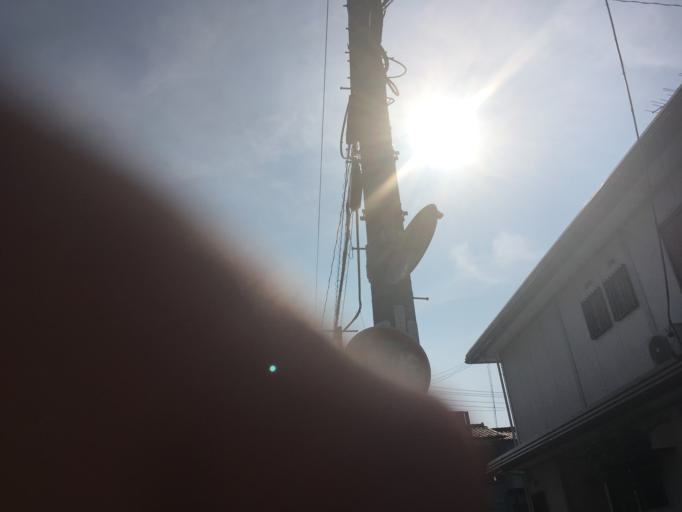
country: JP
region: Kanagawa
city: Minami-rinkan
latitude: 35.4759
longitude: 139.4618
